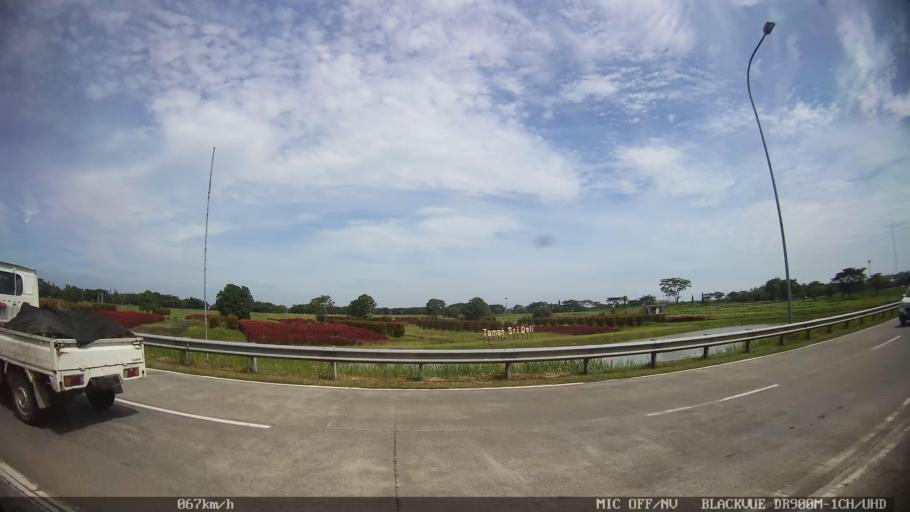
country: ID
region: North Sumatra
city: Percut
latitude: 3.6301
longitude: 98.8761
